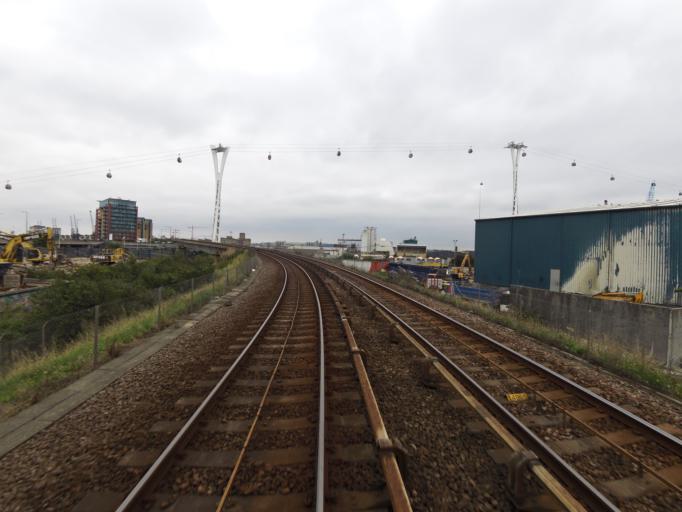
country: GB
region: England
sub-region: Greater London
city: Poplar
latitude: 51.5064
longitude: 0.0131
